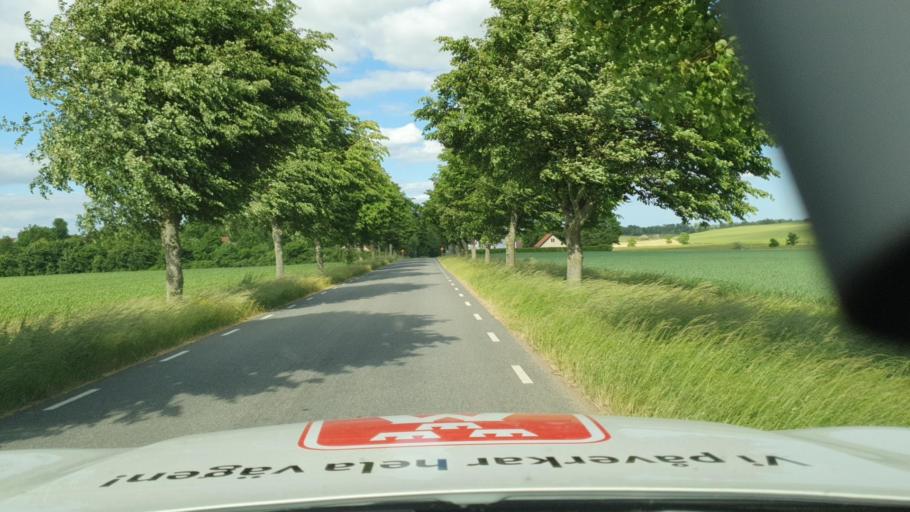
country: SE
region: Skane
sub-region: Tomelilla Kommun
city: Tomelilla
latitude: 55.4877
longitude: 14.0417
